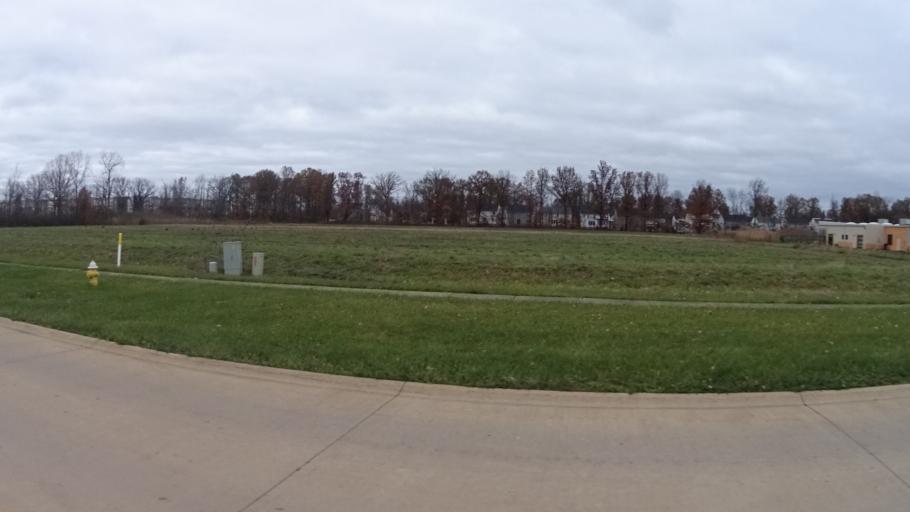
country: US
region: Ohio
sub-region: Lorain County
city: Avon Lake
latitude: 41.4823
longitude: -82.0258
